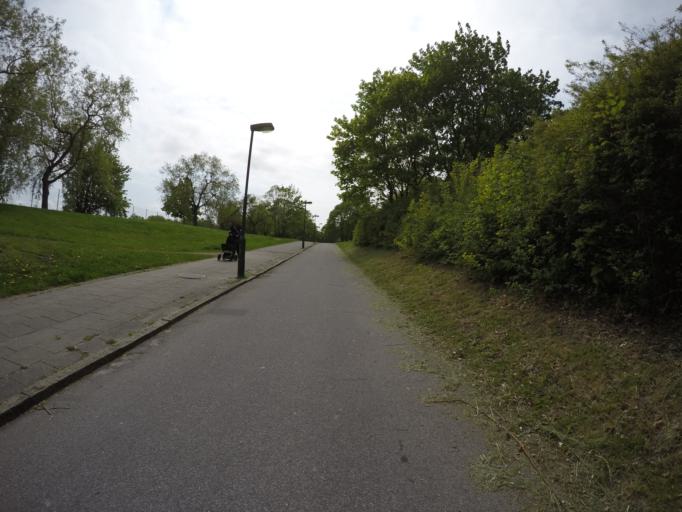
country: SE
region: Skane
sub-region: Malmo
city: Malmoe
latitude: 55.5775
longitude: 12.9798
